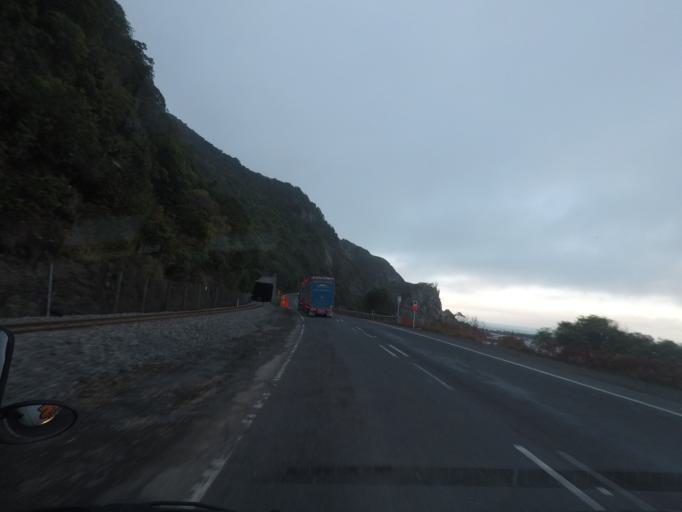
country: NZ
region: Canterbury
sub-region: Kaikoura District
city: Kaikoura
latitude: -42.4503
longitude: 173.5722
